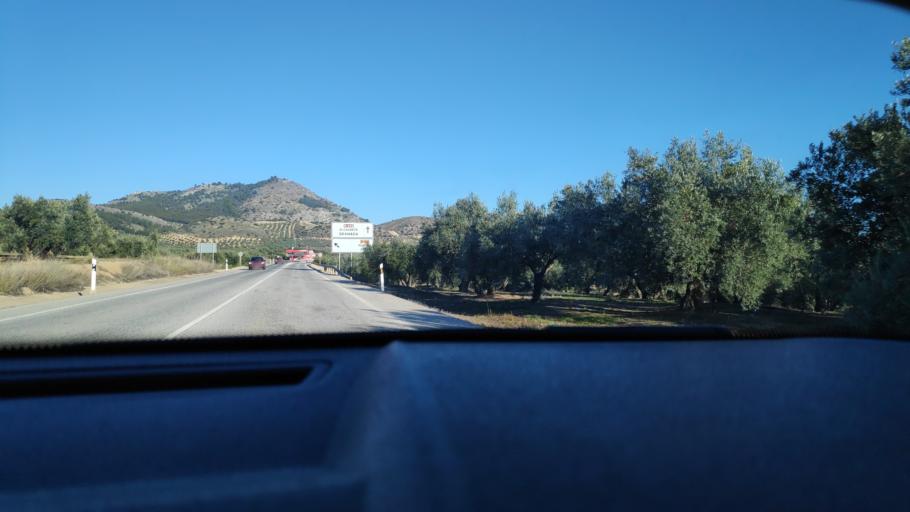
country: ES
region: Andalusia
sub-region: Provincia de Jaen
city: Alcaudete
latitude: 37.5860
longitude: -4.1366
